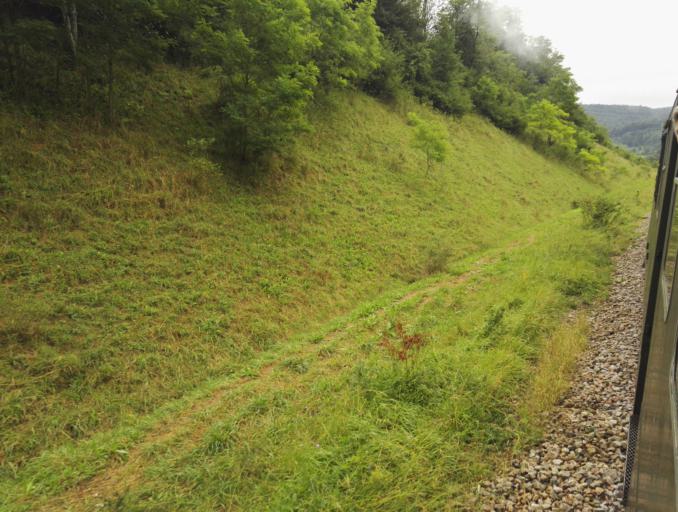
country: DE
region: Baden-Wuerttemberg
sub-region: Freiburg Region
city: Blumberg
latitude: 47.8234
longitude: 8.5547
